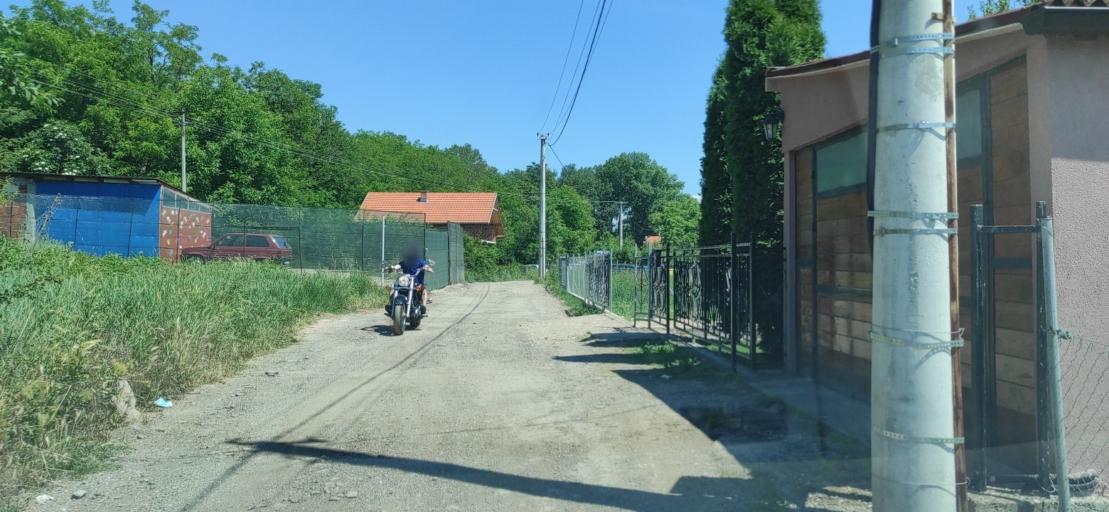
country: RS
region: Central Serbia
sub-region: Nisavski Okrug
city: Nis
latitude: 43.3209
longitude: 21.9540
